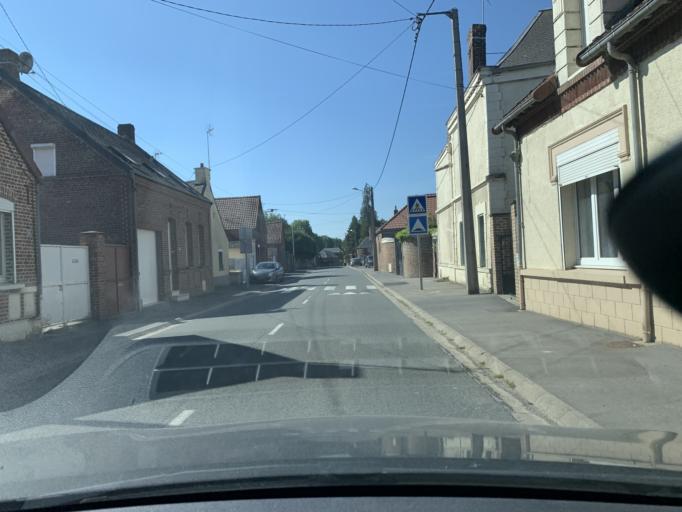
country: FR
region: Nord-Pas-de-Calais
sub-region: Departement du Nord
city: Rumilly-en-Cambresis
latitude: 50.1087
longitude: 3.2486
